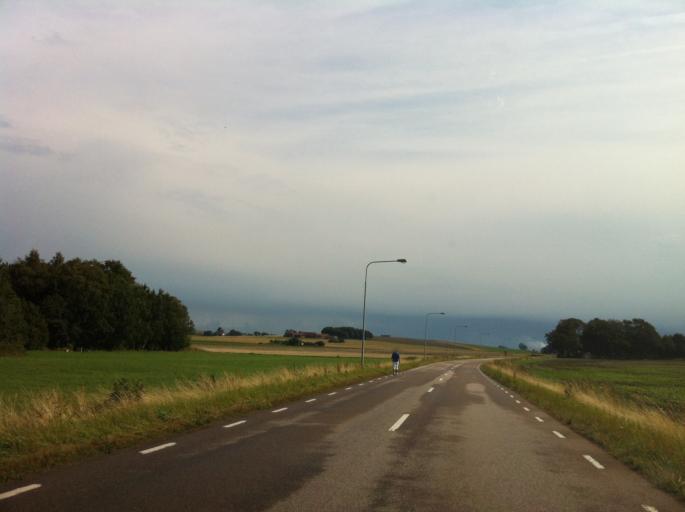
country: SE
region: Skane
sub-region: Helsingborg
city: Glumslov
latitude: 55.9365
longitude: 12.8585
